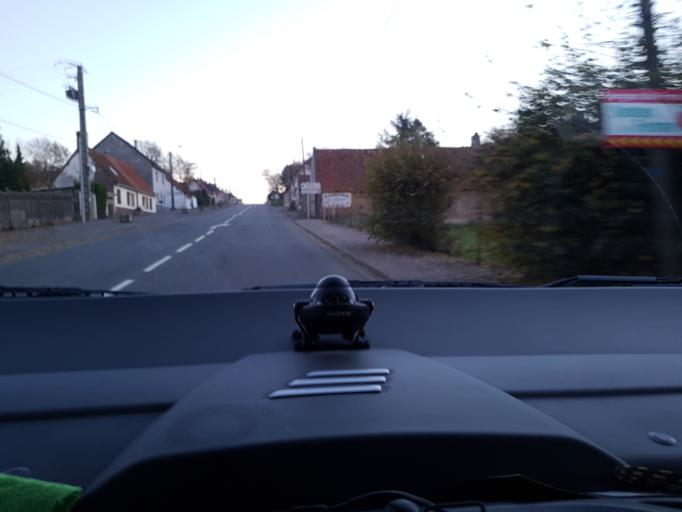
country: FR
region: Picardie
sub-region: Departement de la Somme
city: Rue
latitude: 50.3142
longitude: 1.7504
